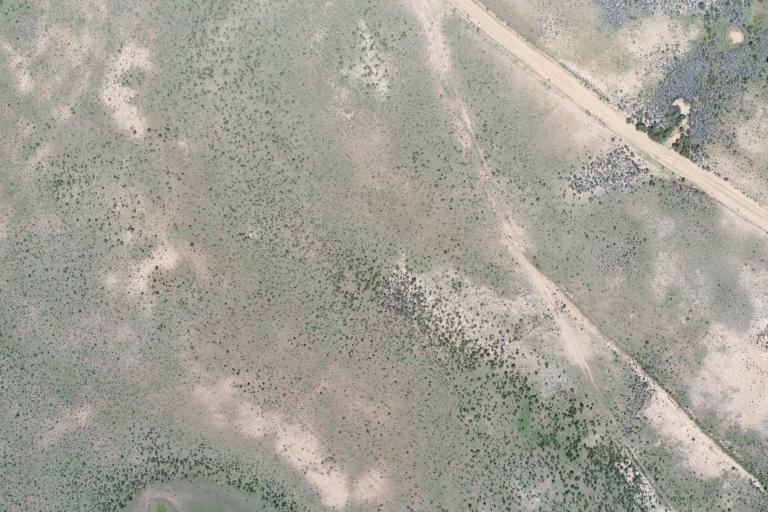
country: BO
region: La Paz
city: Curahuara de Carangas
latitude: -17.2927
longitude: -68.5187
